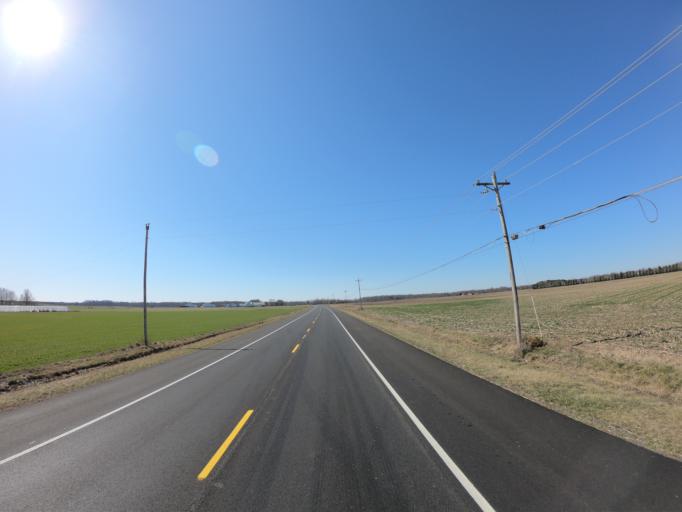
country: US
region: Delaware
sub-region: New Castle County
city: Townsend
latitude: 39.3595
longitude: -75.8293
